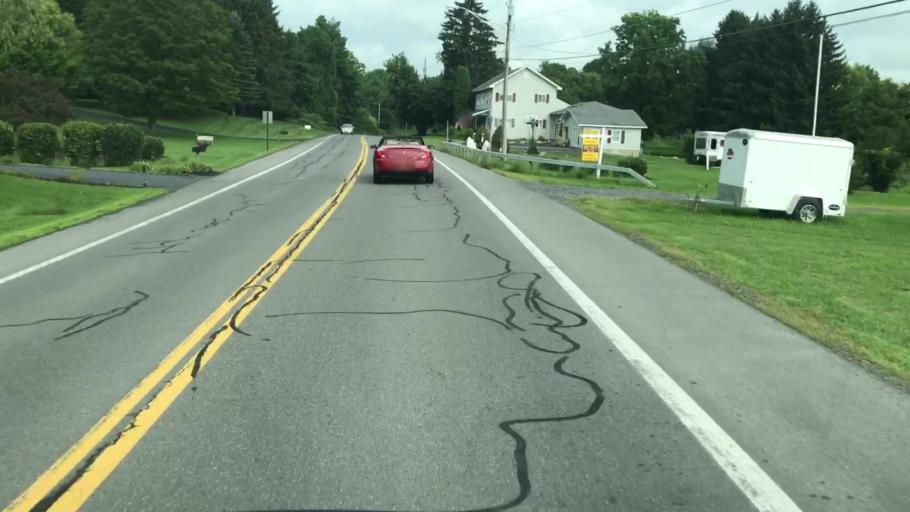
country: US
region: New York
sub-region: Onondaga County
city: Camillus
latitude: 43.0563
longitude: -76.3161
